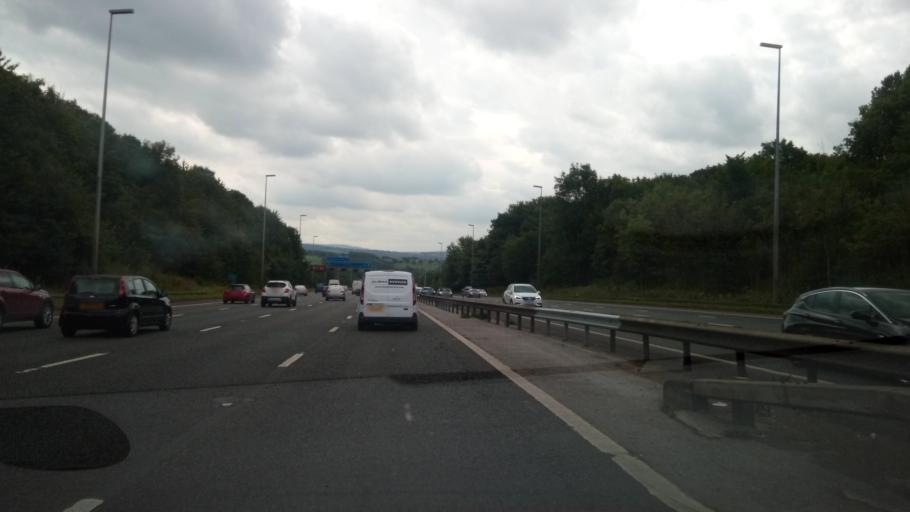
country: GB
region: England
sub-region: Lancashire
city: Goosnargh
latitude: 53.7760
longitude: -2.6440
